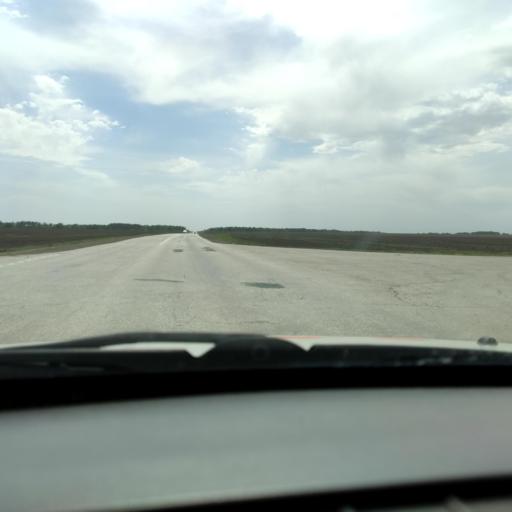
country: RU
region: Samara
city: Yelkhovka
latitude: 53.7203
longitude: 50.2325
